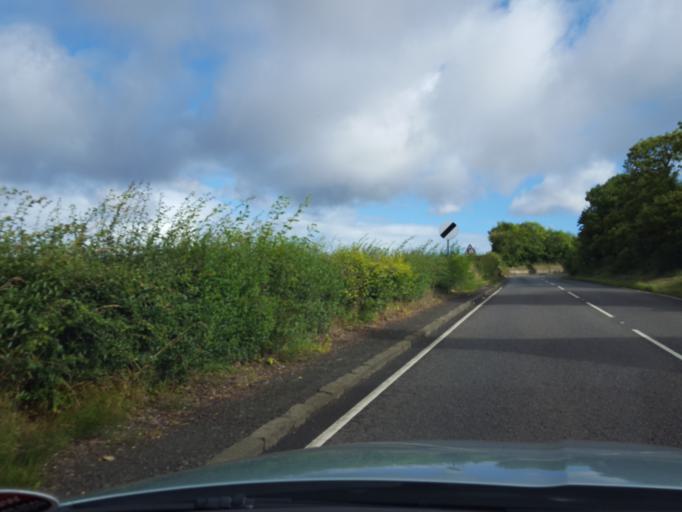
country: GB
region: Scotland
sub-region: West Lothian
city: Linlithgow
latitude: 55.9922
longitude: -3.6132
